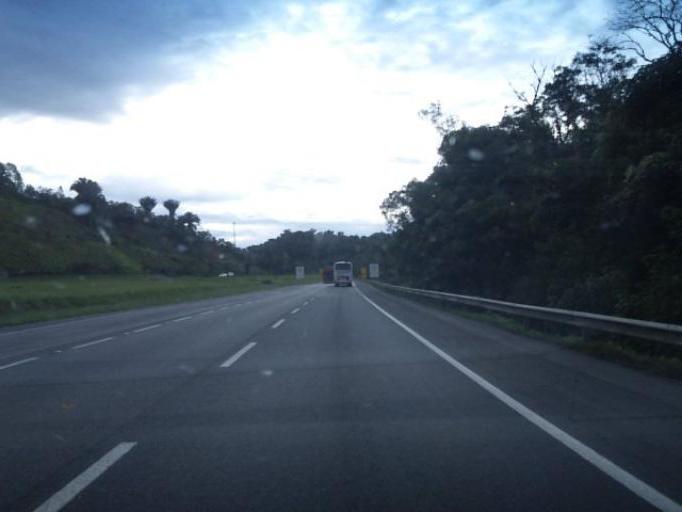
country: BR
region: Parana
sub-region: Antonina
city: Antonina
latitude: -25.0969
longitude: -48.6675
